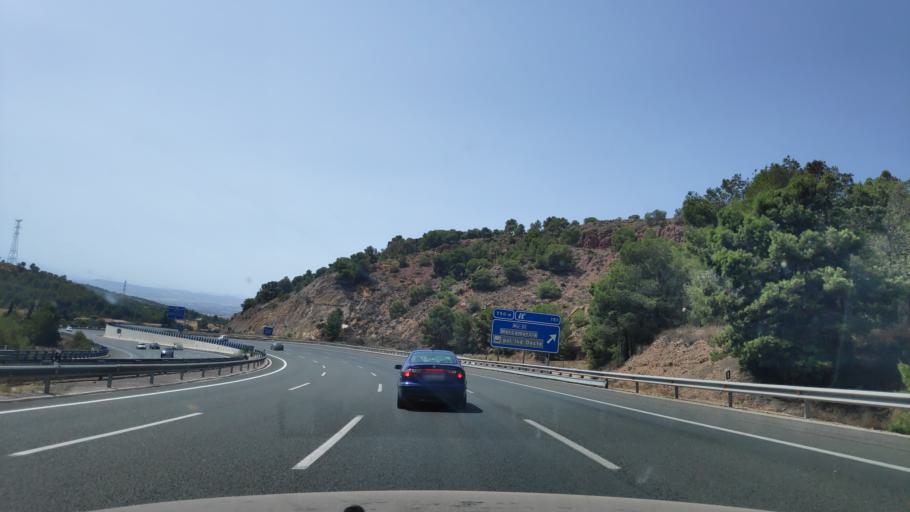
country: ES
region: Murcia
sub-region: Murcia
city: Murcia
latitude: 37.9085
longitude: -1.1576
